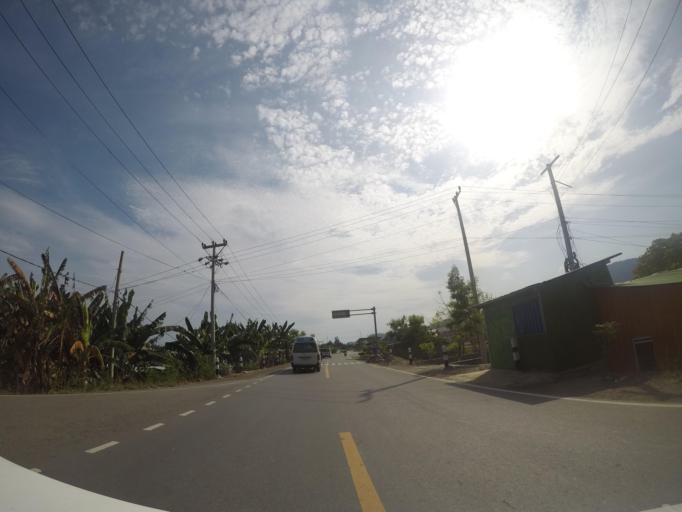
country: ID
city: Metinaro
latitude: -8.5438
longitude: 125.6727
